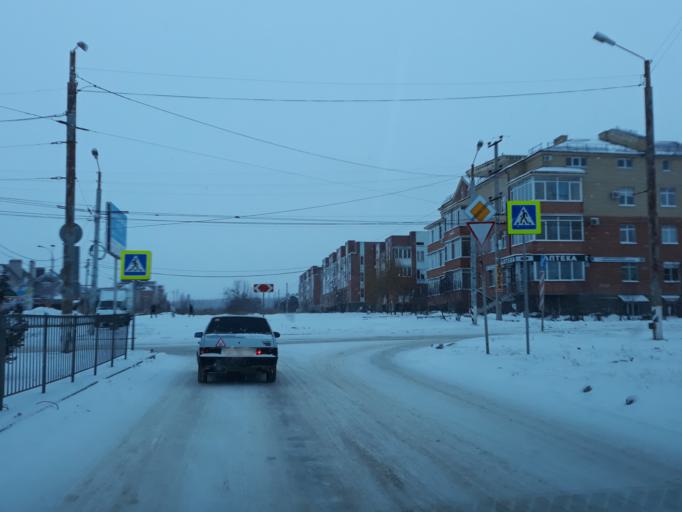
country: RU
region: Rostov
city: Taganrog
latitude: 47.2761
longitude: 38.9163
